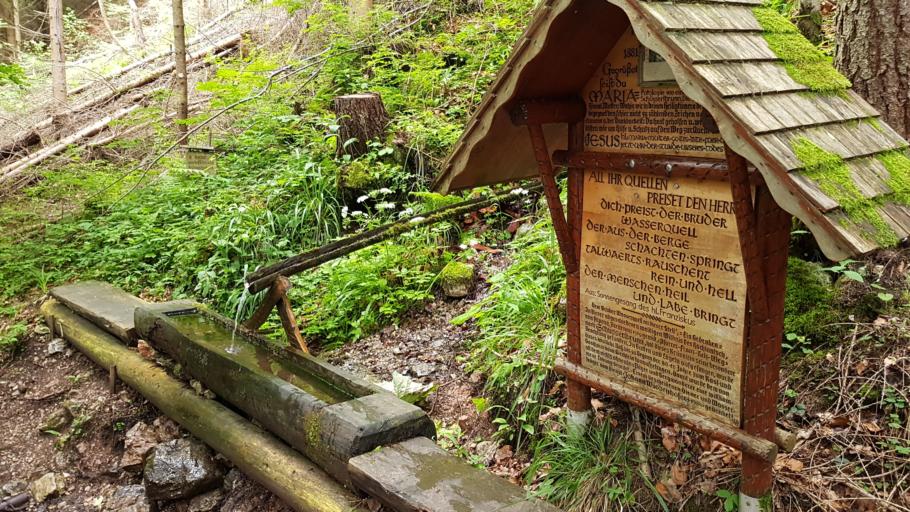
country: AT
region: Styria
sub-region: Politischer Bezirk Graz-Umgebung
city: Rothelstein
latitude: 47.3649
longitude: 15.4166
